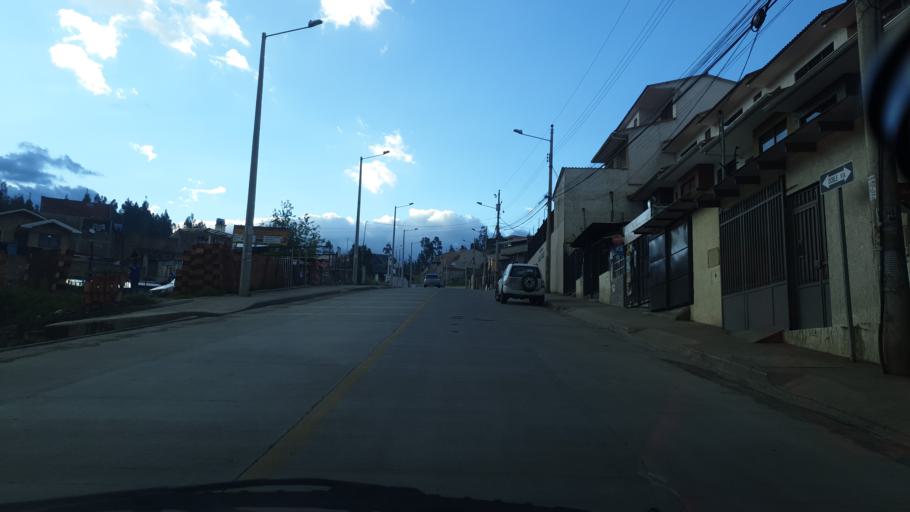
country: EC
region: Azuay
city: Cuenca
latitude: -2.8845
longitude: -79.0441
